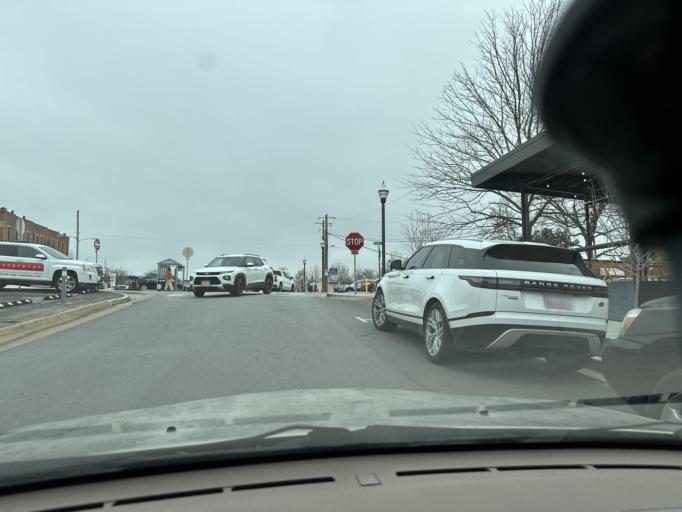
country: US
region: Arkansas
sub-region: Washington County
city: Fayetteville
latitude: 36.0630
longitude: -94.1618
